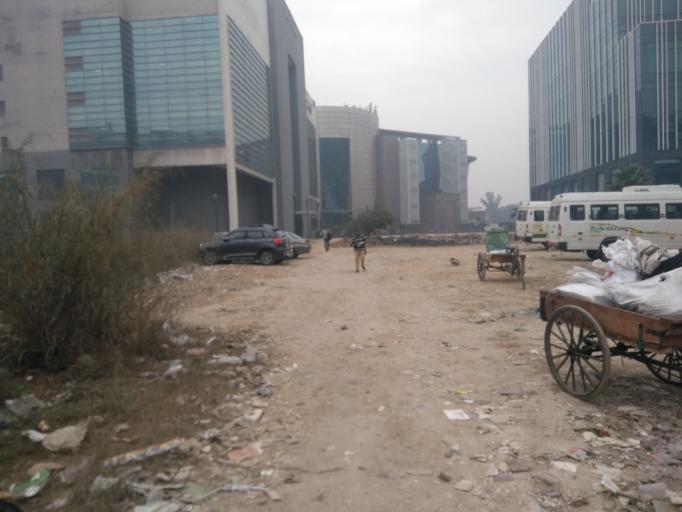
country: IN
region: Uttar Pradesh
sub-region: Gautam Buddha Nagar
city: Noida
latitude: 28.5384
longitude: 77.2879
